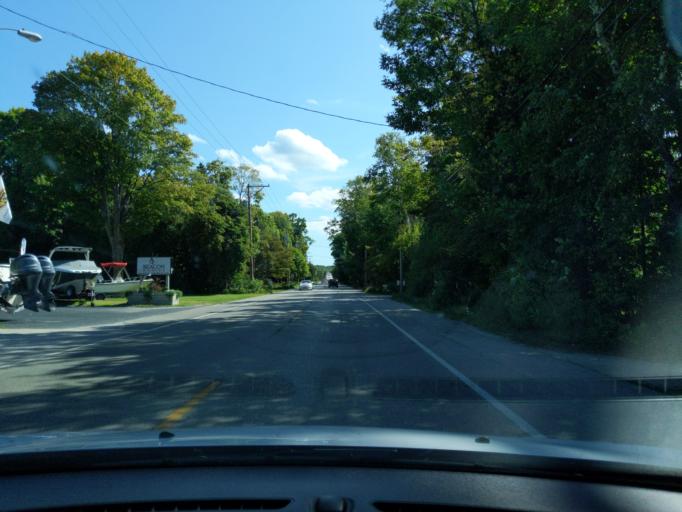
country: US
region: Wisconsin
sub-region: Door County
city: Sturgeon Bay
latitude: 45.1996
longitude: -87.1189
